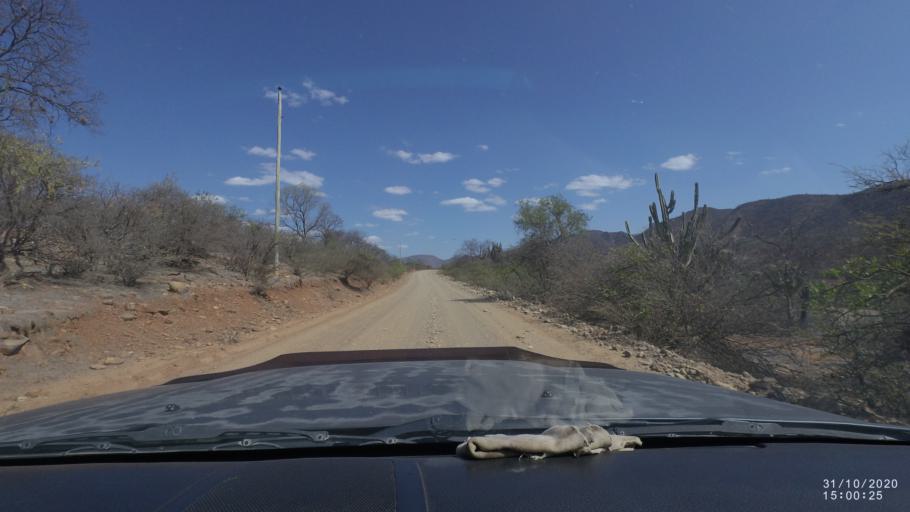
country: BO
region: Cochabamba
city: Aiquile
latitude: -18.2573
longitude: -64.8250
